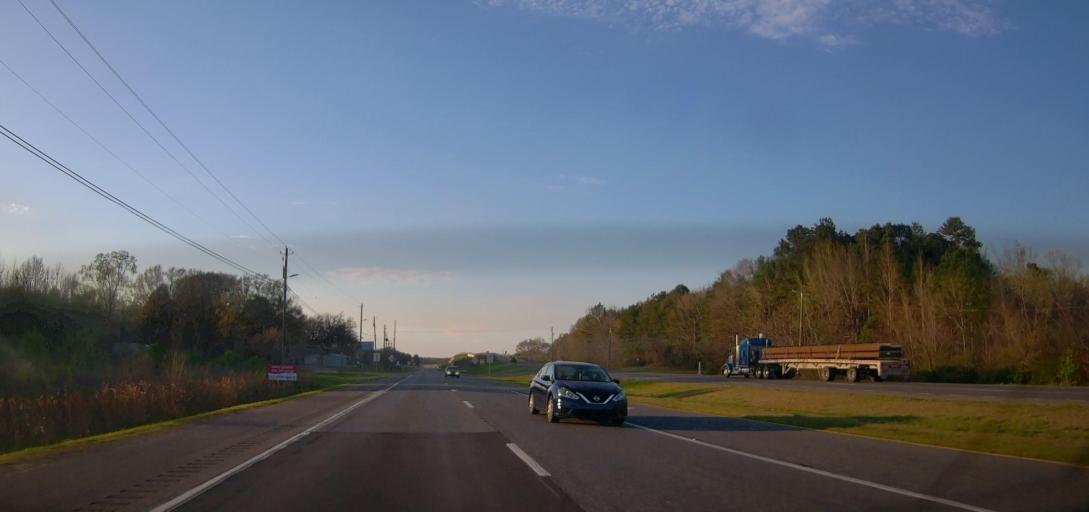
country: US
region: Alabama
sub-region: Talladega County
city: Childersburg
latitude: 33.2863
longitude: -86.3634
